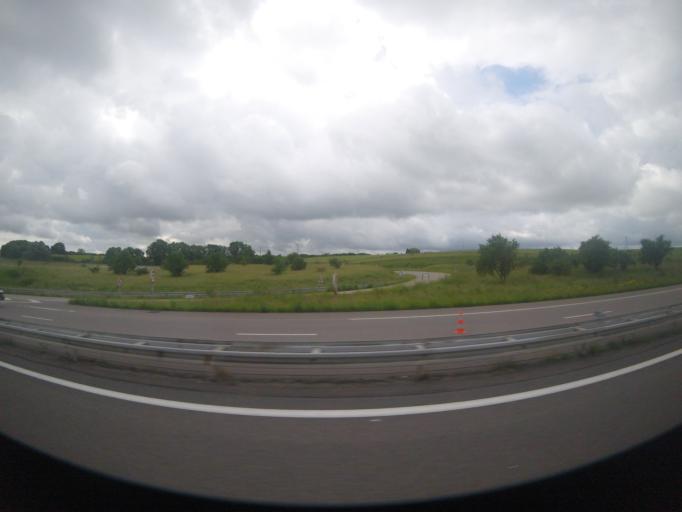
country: FR
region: Lorraine
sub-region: Departement de Meurthe-et-Moselle
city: Giraumont
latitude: 49.1986
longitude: 5.8978
